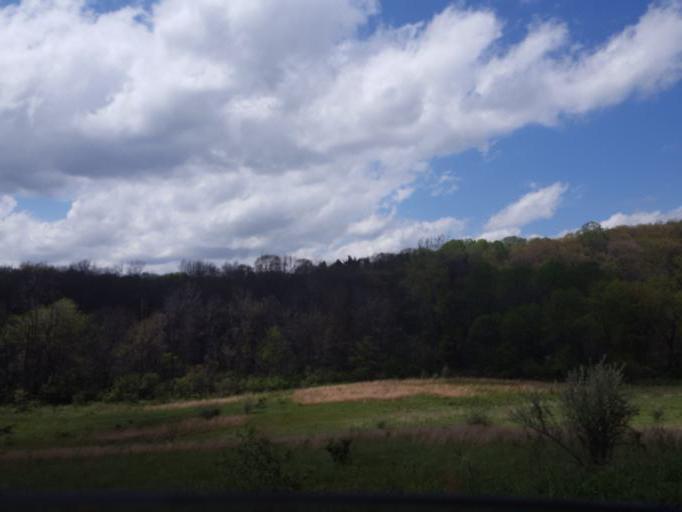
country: US
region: Ohio
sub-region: Richland County
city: Lexington
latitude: 40.7167
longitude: -82.5744
